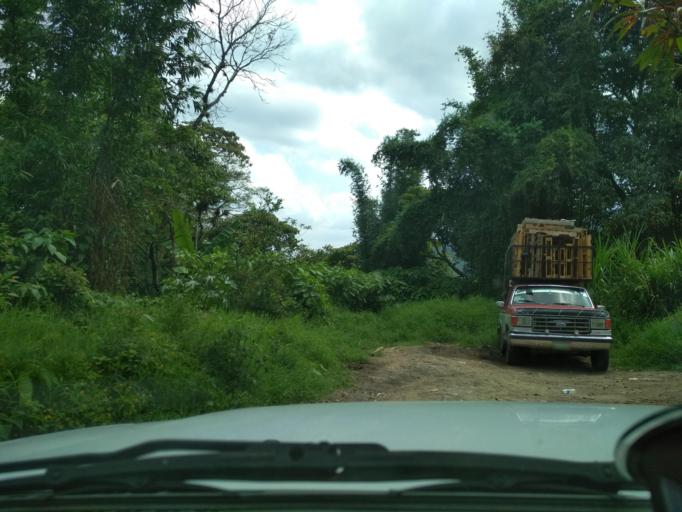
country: MX
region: Veracruz
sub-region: Fortin
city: Monte Salas
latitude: 18.9359
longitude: -97.0197
